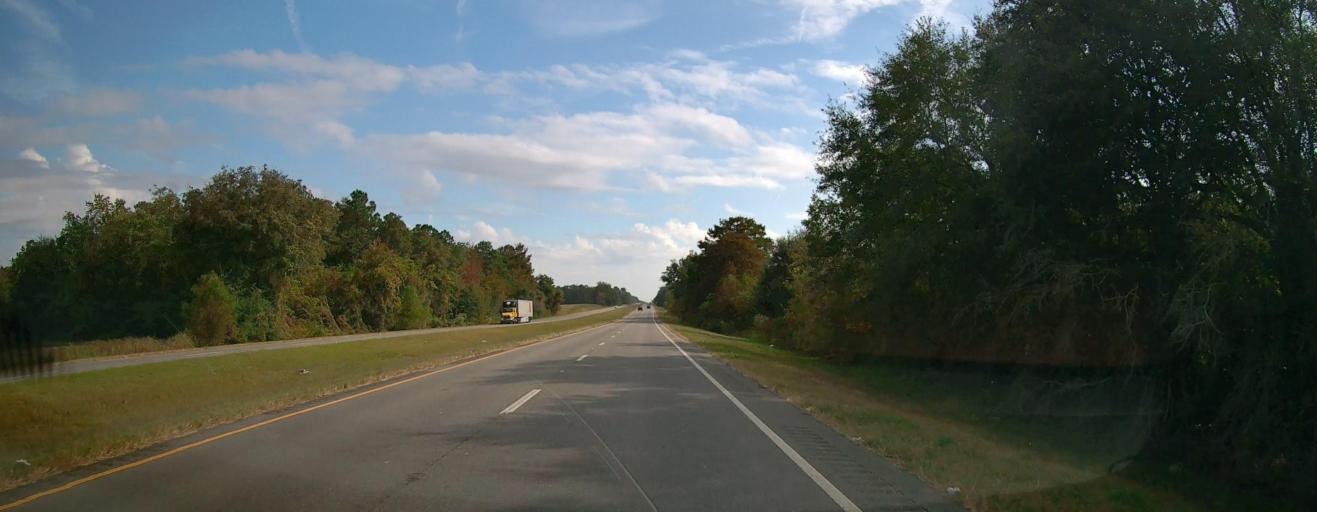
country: US
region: Georgia
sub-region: Thomas County
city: Meigs
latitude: 31.0216
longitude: -84.0581
